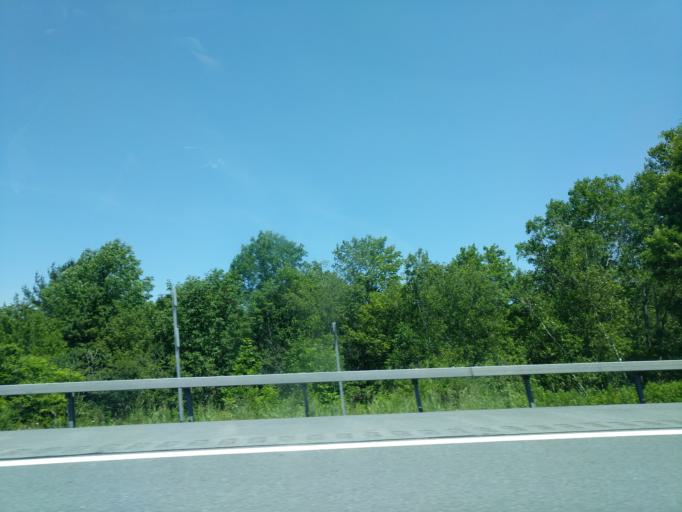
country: US
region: New York
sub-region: Sullivan County
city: Livingston Manor
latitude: 41.9231
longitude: -74.8403
